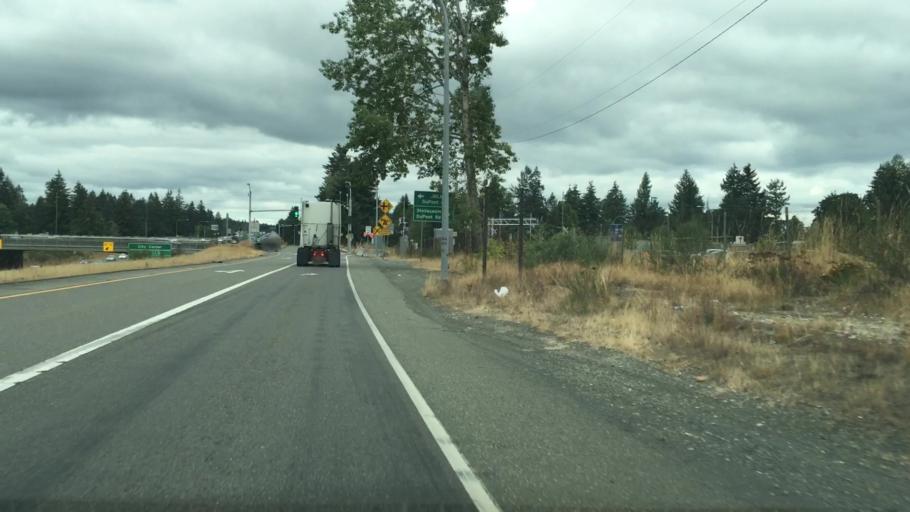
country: US
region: Washington
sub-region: Pierce County
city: DuPont
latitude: 47.0936
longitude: -122.6226
